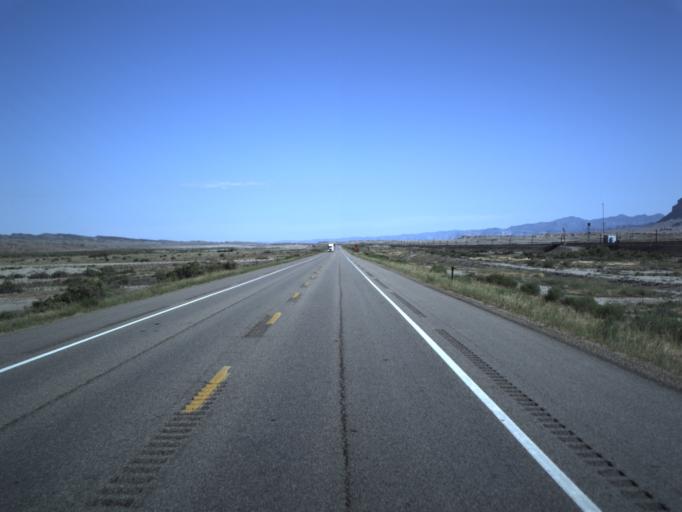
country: US
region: Utah
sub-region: Carbon County
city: East Carbon City
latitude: 39.0945
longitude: -110.3217
